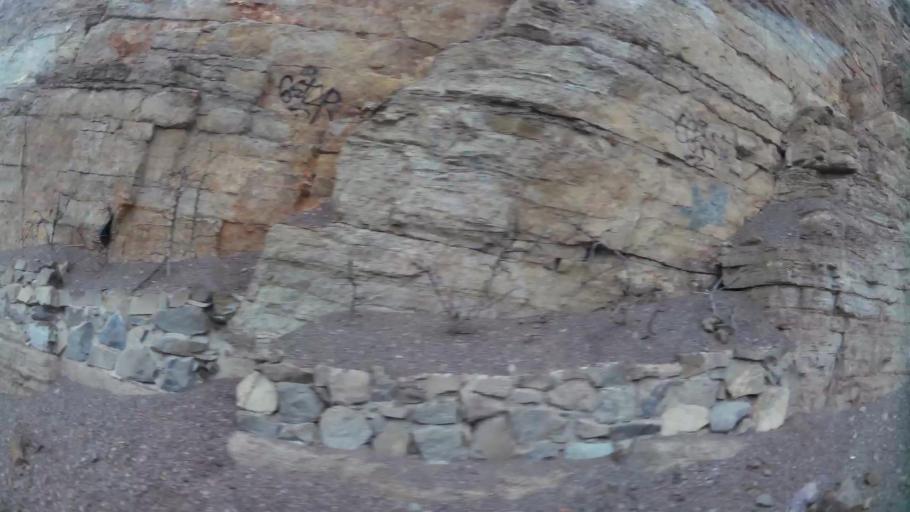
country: PE
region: Lima
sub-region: Lima
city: Surco
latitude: -12.1678
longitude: -77.0366
